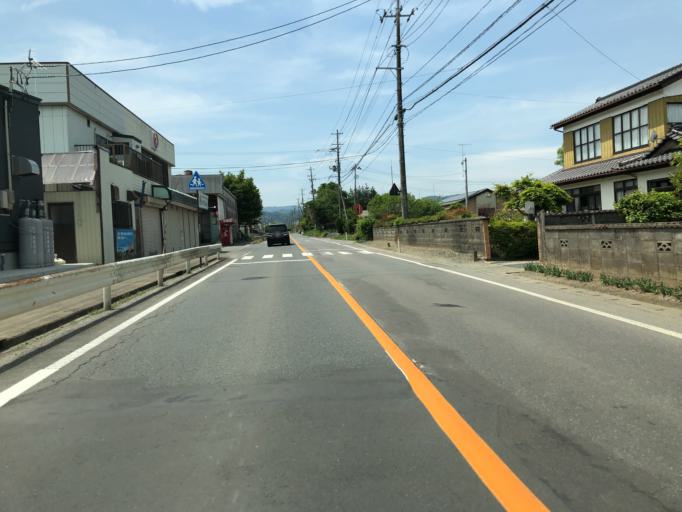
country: JP
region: Fukushima
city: Namie
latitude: 37.6969
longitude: 140.9559
